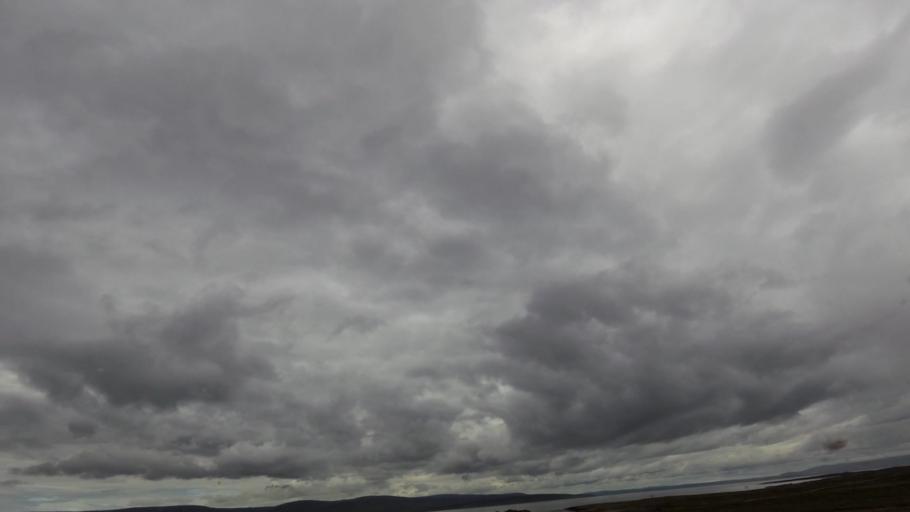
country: IS
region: West
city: Stykkisholmur
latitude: 65.0223
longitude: -22.2140
